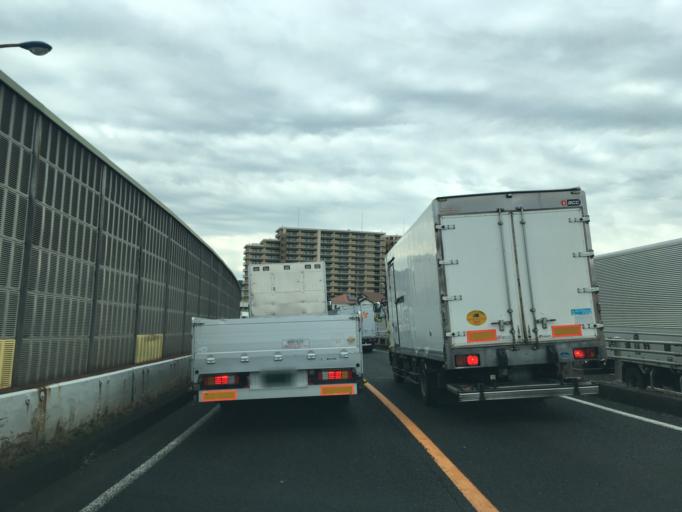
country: JP
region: Tokyo
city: Hachioji
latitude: 35.6616
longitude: 139.3532
